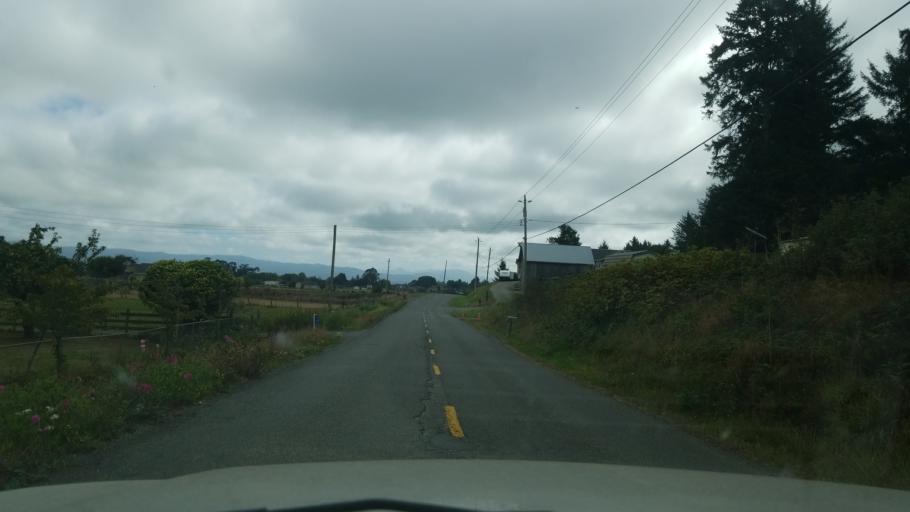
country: US
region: California
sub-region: Humboldt County
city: Ferndale
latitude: 40.5807
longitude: -124.2765
